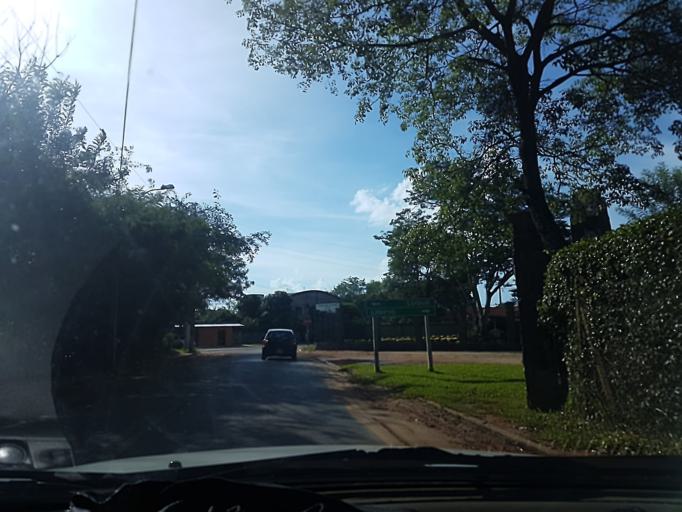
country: PY
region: Central
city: Limpio
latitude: -25.1912
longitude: -57.4630
